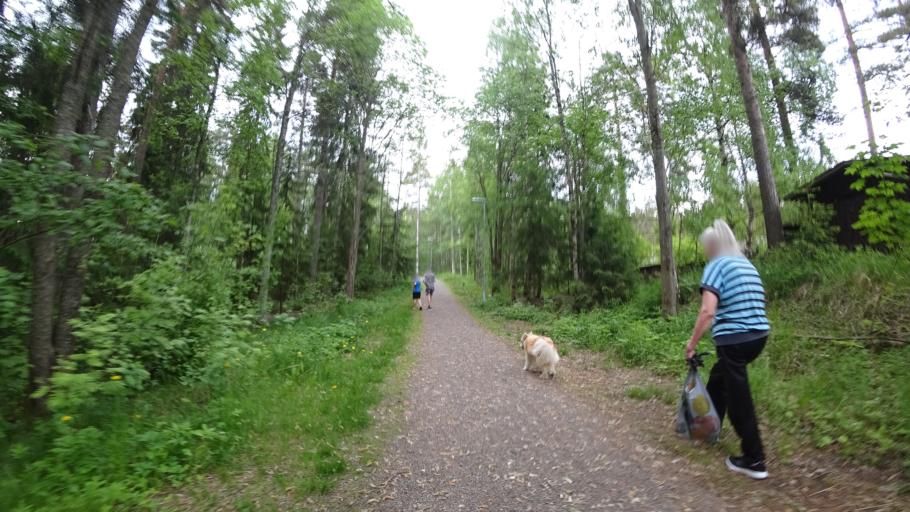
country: FI
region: Pirkanmaa
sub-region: Tampere
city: Yloejaervi
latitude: 61.5196
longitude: 23.6068
